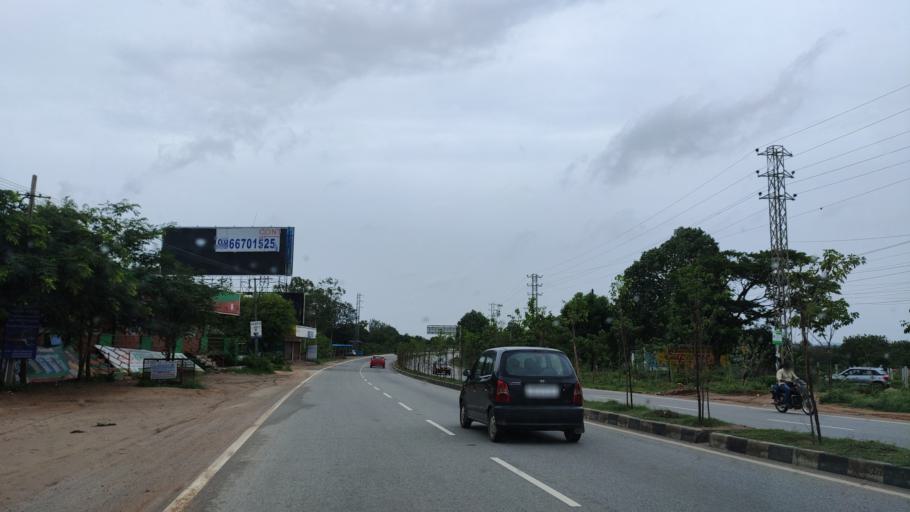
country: IN
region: Telangana
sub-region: Rangareddi
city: Secunderabad
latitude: 17.5996
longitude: 78.5680
